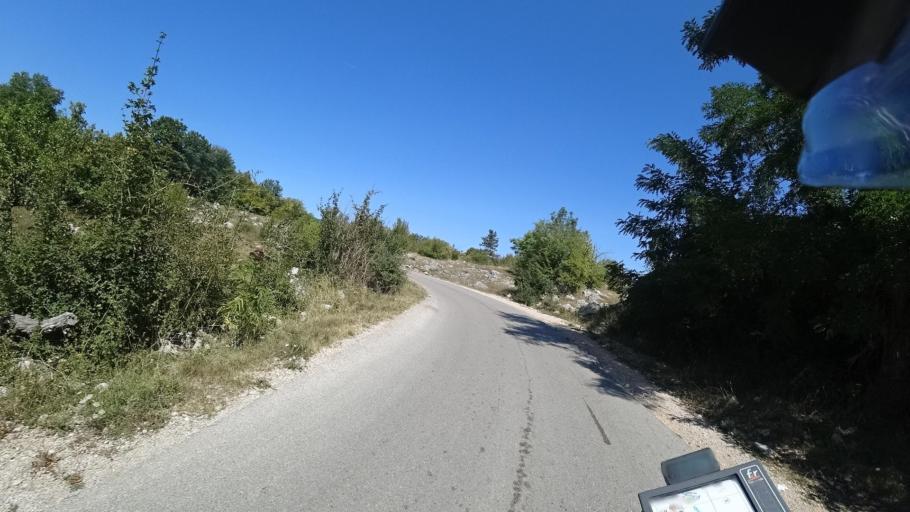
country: HR
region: Licko-Senjska
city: Popovaca
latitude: 44.7288
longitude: 15.2926
